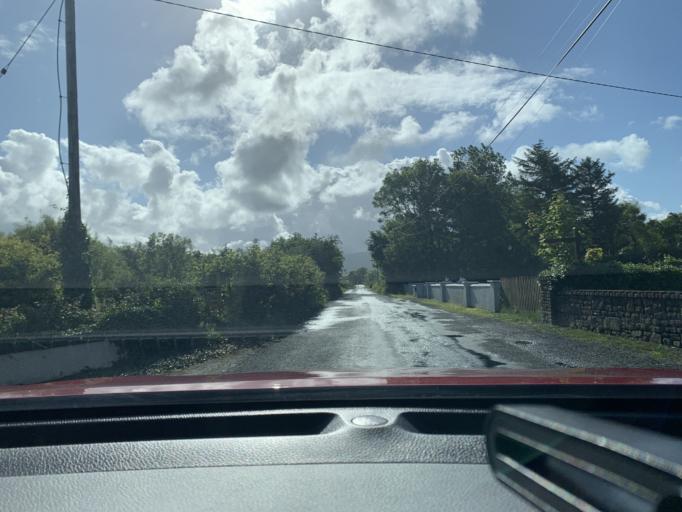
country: IE
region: Connaught
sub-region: Sligo
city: Strandhill
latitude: 54.3925
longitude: -8.5486
